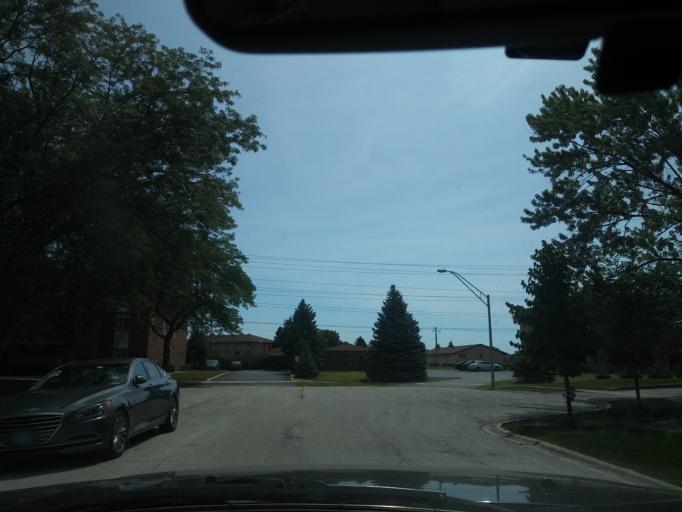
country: US
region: Illinois
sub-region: Cook County
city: Tinley Park
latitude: 41.6151
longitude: -87.8006
